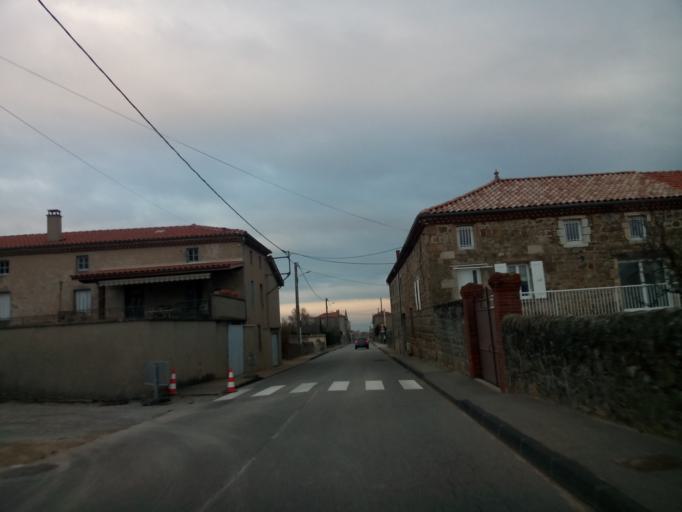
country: FR
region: Rhone-Alpes
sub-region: Departement de la Loire
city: Maclas
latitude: 45.3594
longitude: 4.6796
